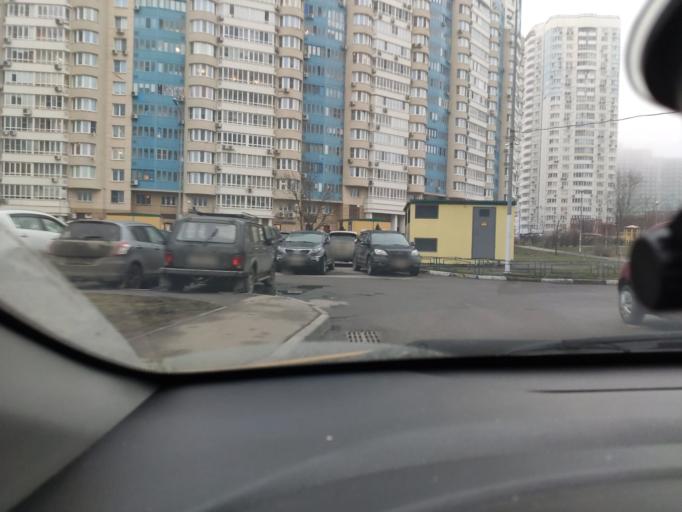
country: RU
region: Moscow
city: Chertanovo Yuzhnoye
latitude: 55.5943
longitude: 37.5965
